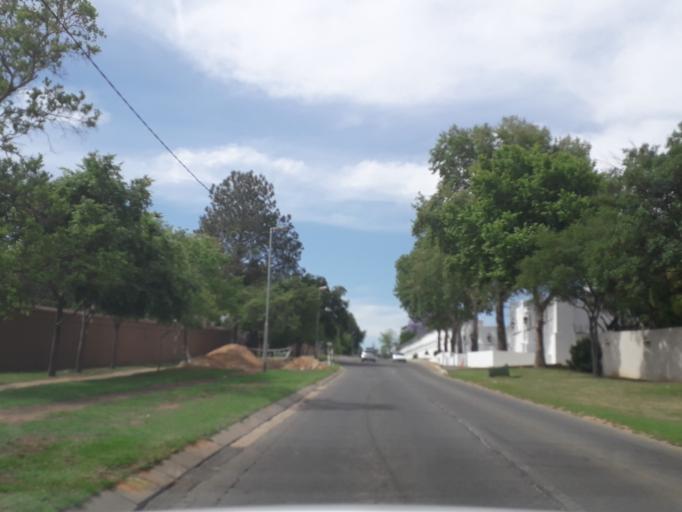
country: ZA
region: Gauteng
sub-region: City of Johannesburg Metropolitan Municipality
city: Diepsloot
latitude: -26.0591
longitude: 28.0134
